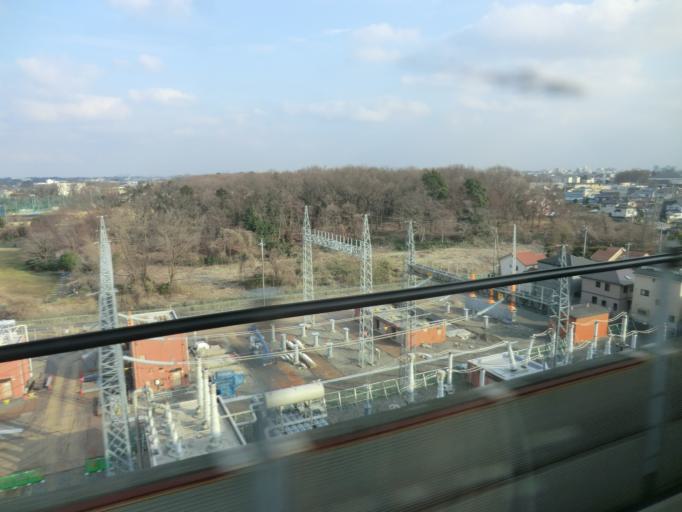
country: JP
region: Saitama
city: Ageoshimo
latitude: 35.9725
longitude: 139.6242
